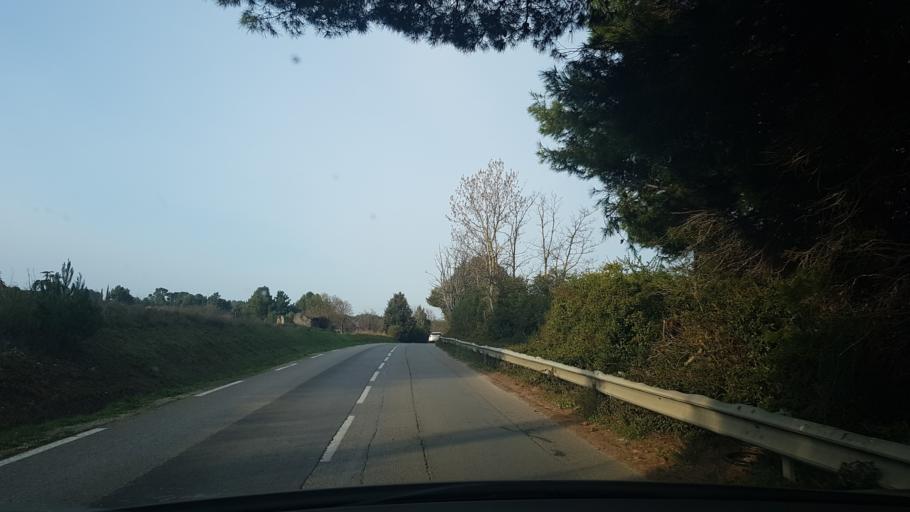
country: FR
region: Provence-Alpes-Cote d'Azur
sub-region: Departement des Bouches-du-Rhone
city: Bouc-Bel-Air
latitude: 43.5031
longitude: 5.3958
